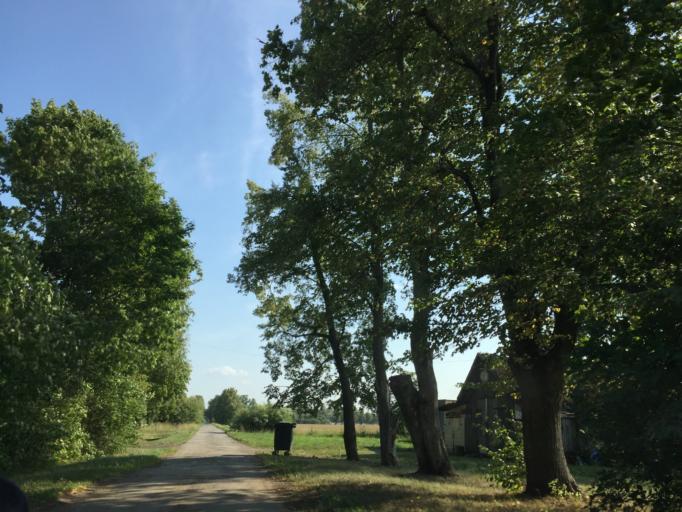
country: LV
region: Jelgava
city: Jelgava
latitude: 56.4543
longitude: 23.6811
